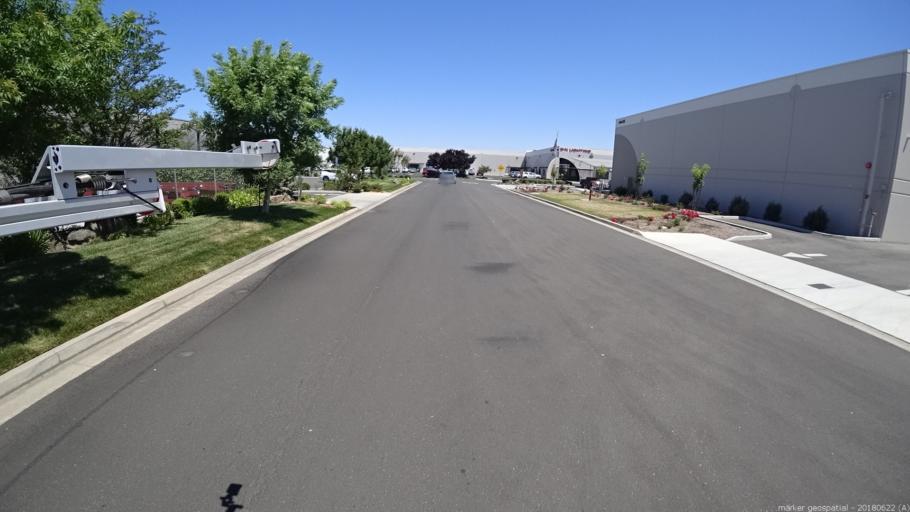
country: US
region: California
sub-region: Madera County
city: Bonadelle Ranchos-Madera Ranchos
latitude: 36.8970
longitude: -119.8123
